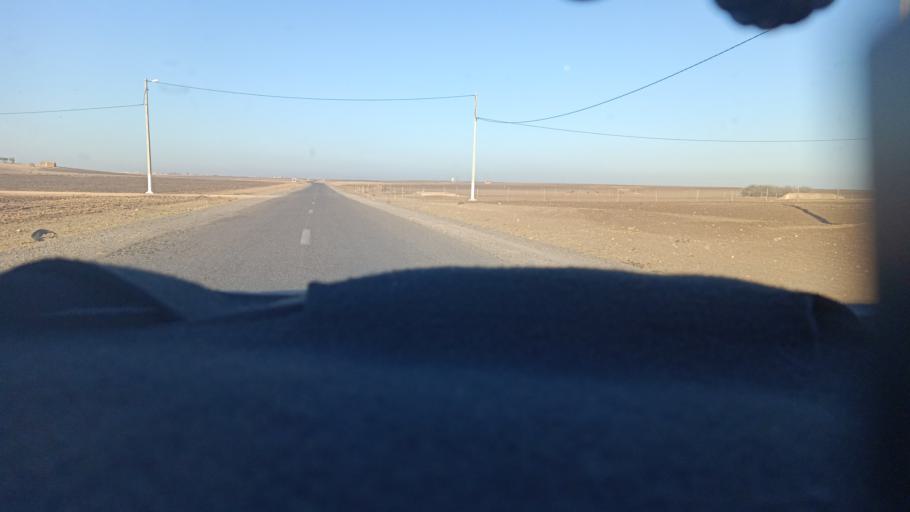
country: MA
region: Doukkala-Abda
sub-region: Safi
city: Youssoufia
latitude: 32.3710
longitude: -8.7240
